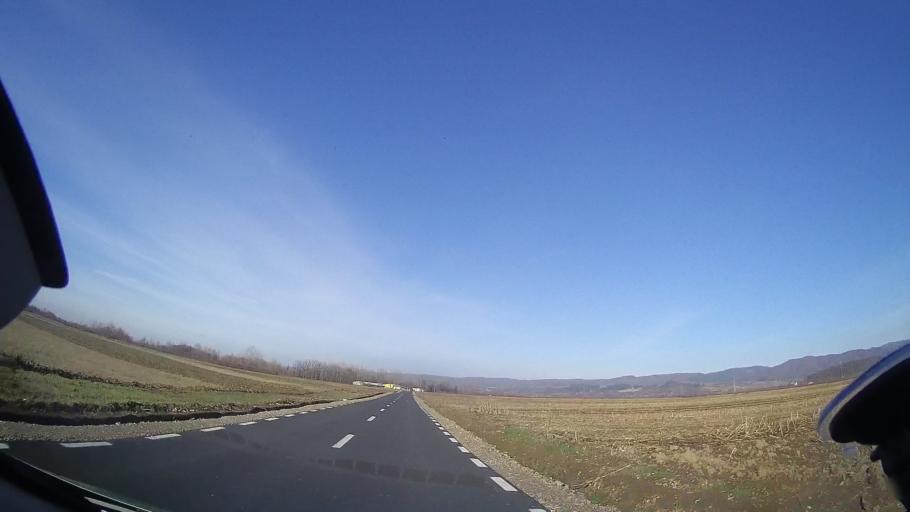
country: RO
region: Bihor
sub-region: Comuna Vadu Crisului
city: Vadu Crisului
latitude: 46.9980
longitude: 22.5052
